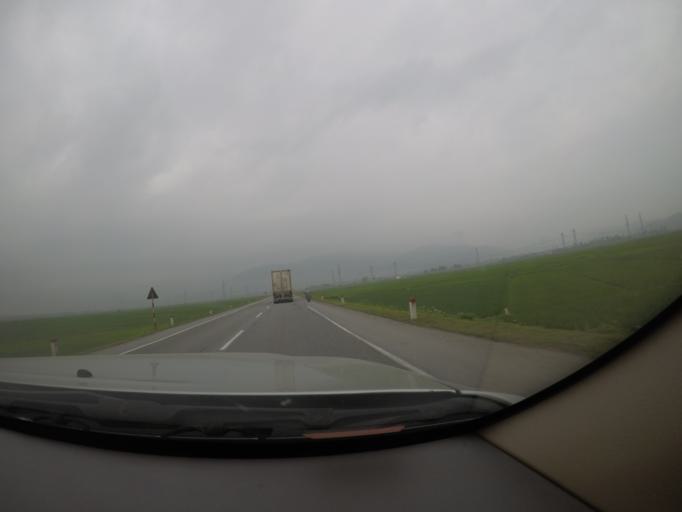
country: VN
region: Ha Tinh
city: Ky Anh
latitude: 18.1032
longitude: 106.2638
